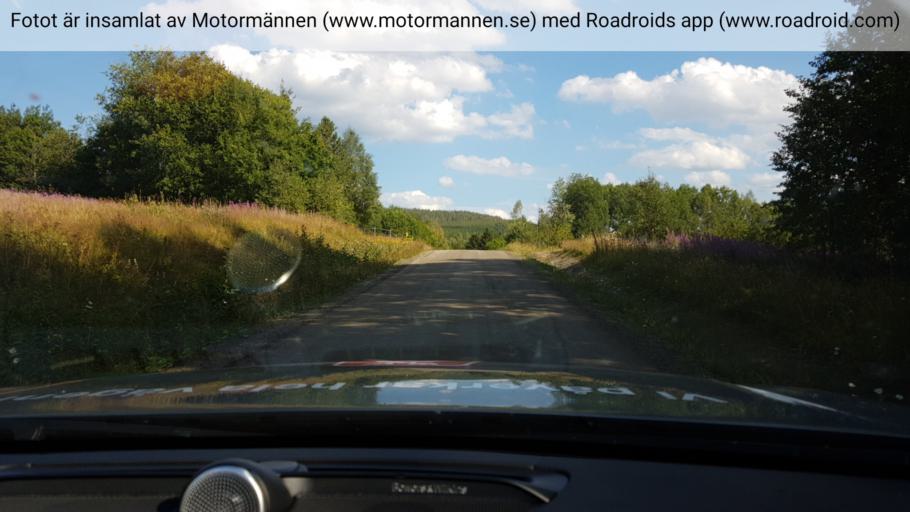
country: SE
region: Jaemtland
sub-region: Stroemsunds Kommun
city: Stroemsund
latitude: 63.9919
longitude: 15.9938
